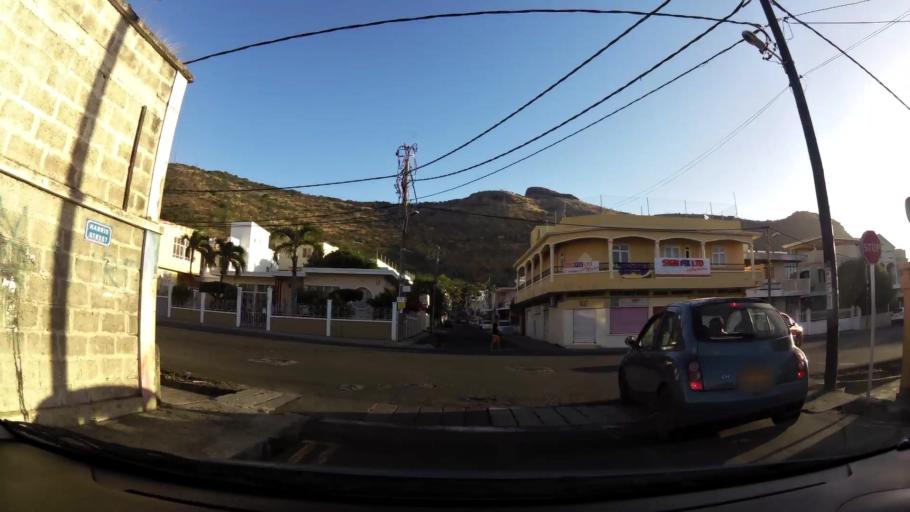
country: MU
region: Port Louis
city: Port Louis
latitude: -20.1725
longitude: 57.5051
